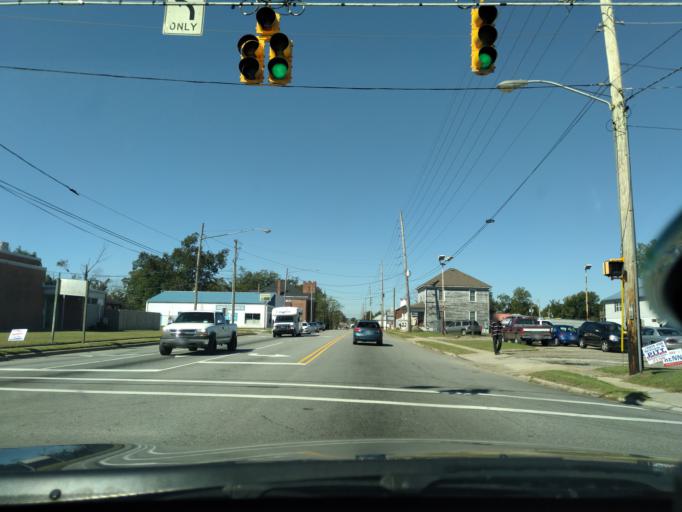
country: US
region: North Carolina
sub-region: Beaufort County
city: Washington
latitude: 35.5466
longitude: -77.0519
